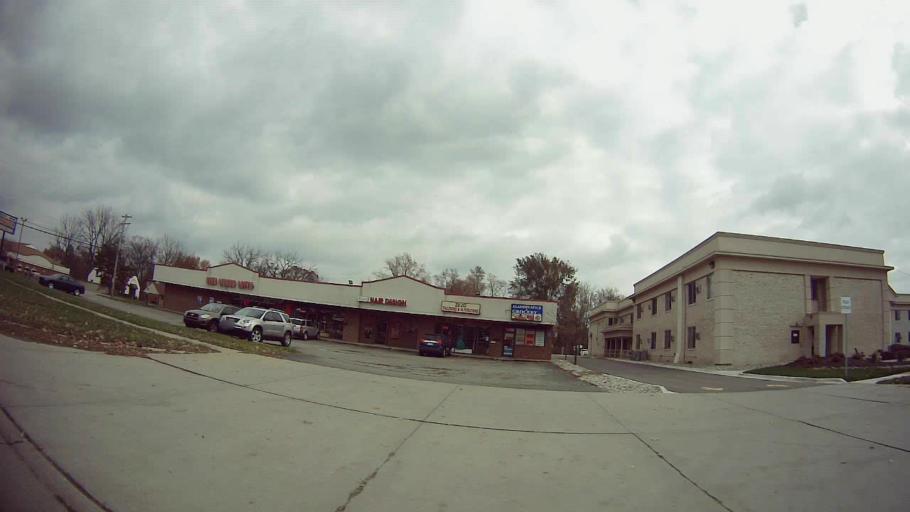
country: US
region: Michigan
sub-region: Oakland County
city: Madison Heights
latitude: 42.5268
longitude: -83.0681
